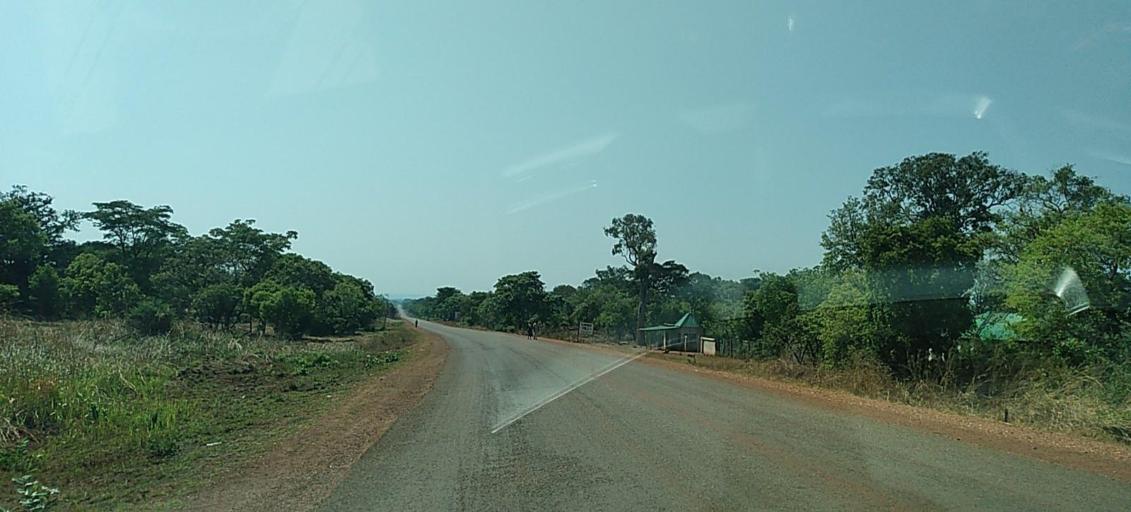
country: ZM
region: North-Western
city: Solwezi
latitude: -12.1175
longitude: 25.5091
